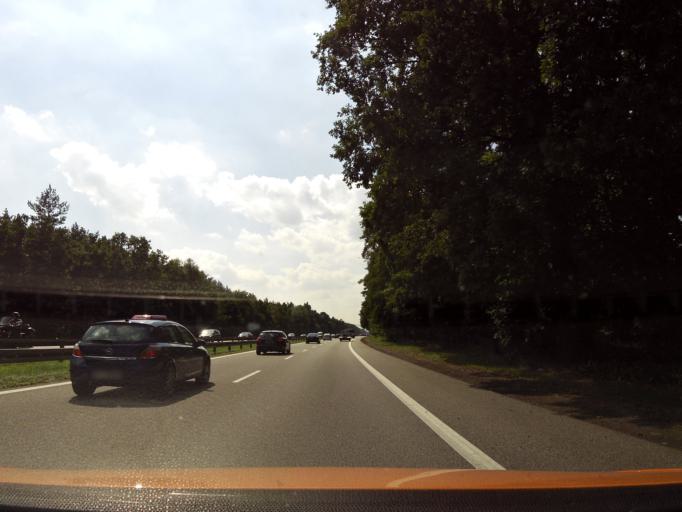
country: PL
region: West Pomeranian Voivodeship
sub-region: Powiat goleniowski
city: Goleniow
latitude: 53.4541
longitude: 14.7872
